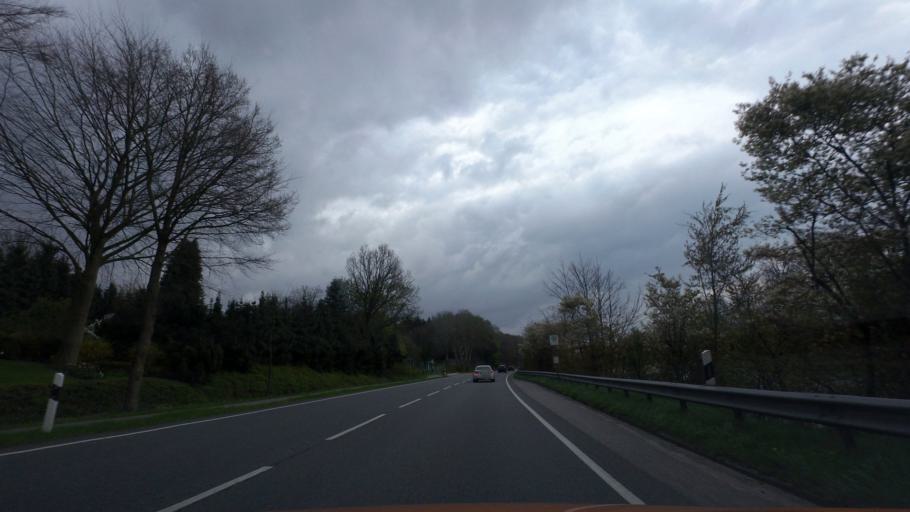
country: DE
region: Lower Saxony
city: Wardenburg
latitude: 53.1027
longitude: 8.1036
